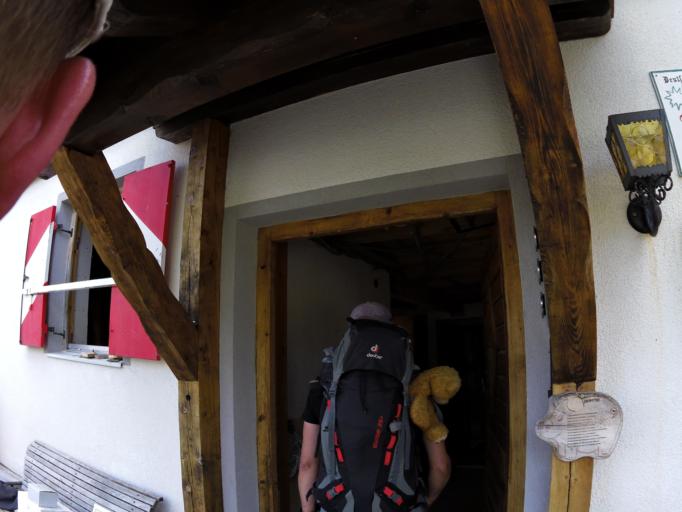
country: AT
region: Tyrol
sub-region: Politischer Bezirk Innsbruck Land
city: Gschnitz
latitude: 47.0433
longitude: 11.3109
